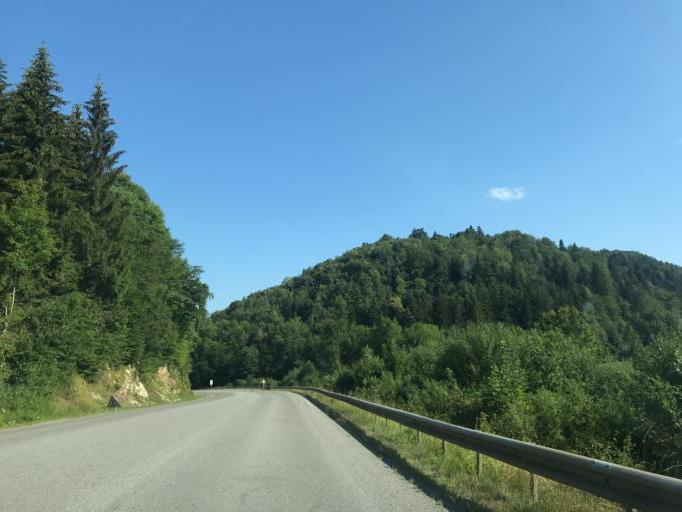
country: FR
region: Franche-Comte
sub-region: Departement du Jura
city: Moirans-en-Montagne
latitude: 46.3928
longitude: 5.7393
